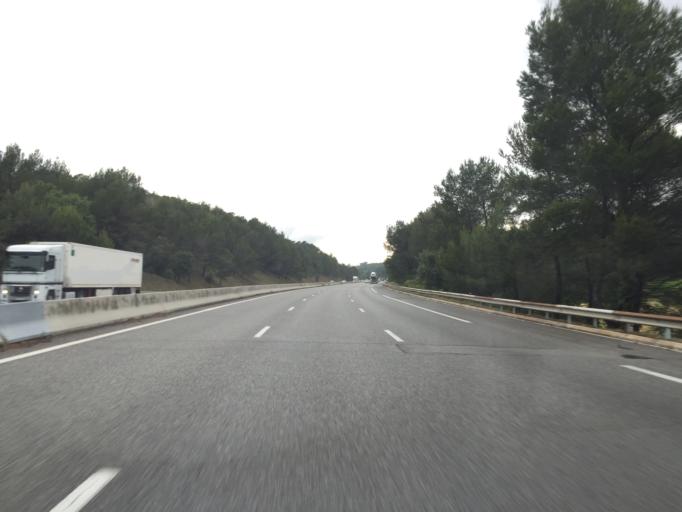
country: FR
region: Provence-Alpes-Cote d'Azur
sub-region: Departement du Var
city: Cabasse
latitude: 43.4071
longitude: 6.1862
